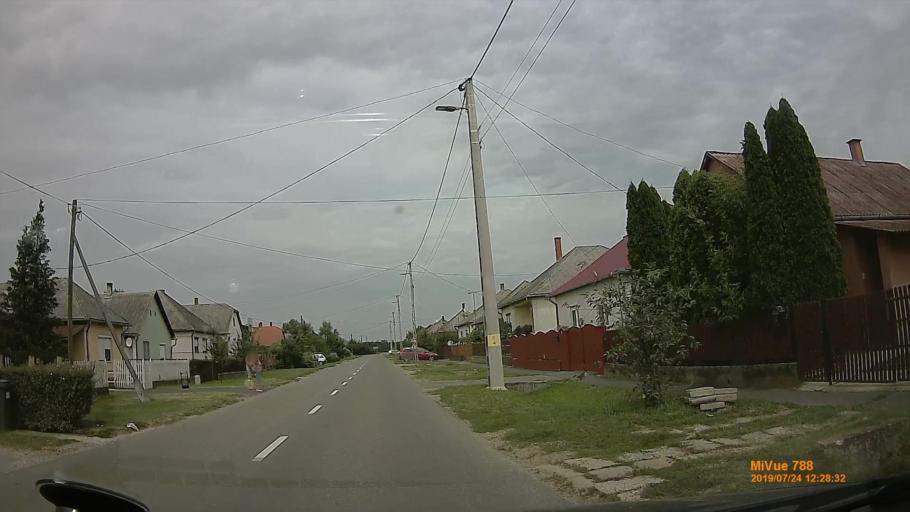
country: HU
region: Szabolcs-Szatmar-Bereg
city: Vasarosnameny
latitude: 48.1427
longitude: 22.3453
